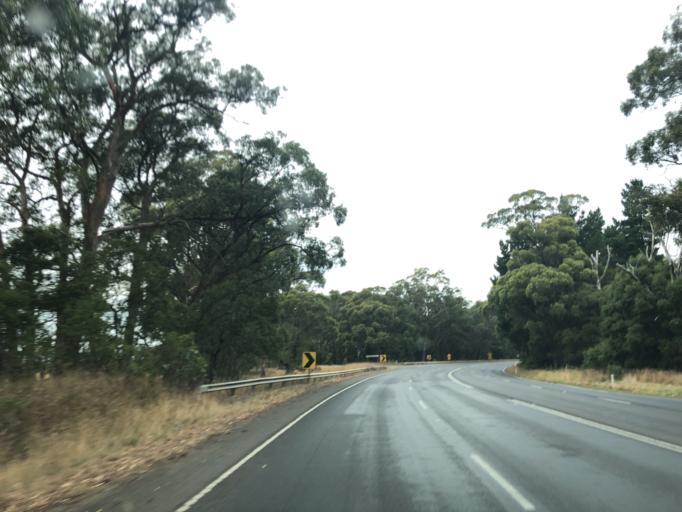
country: AU
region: Victoria
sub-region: Hume
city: Sunbury
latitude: -37.4039
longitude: 144.5362
